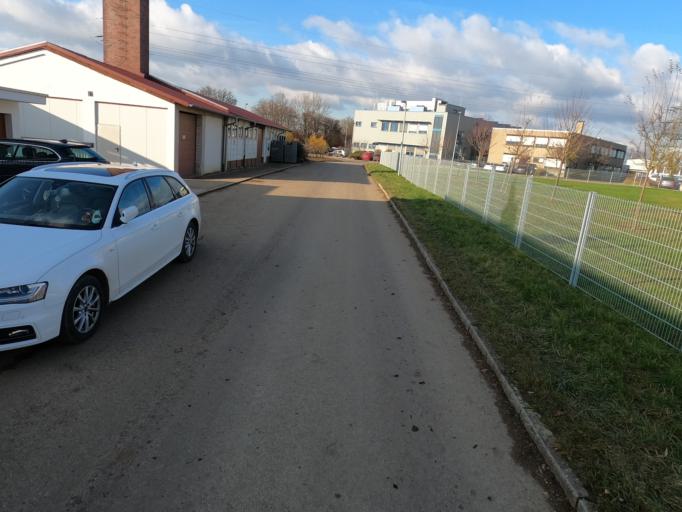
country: DE
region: Baden-Wuerttemberg
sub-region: Regierungsbezirk Stuttgart
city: Hattenhofen
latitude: 48.6638
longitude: 9.5549
